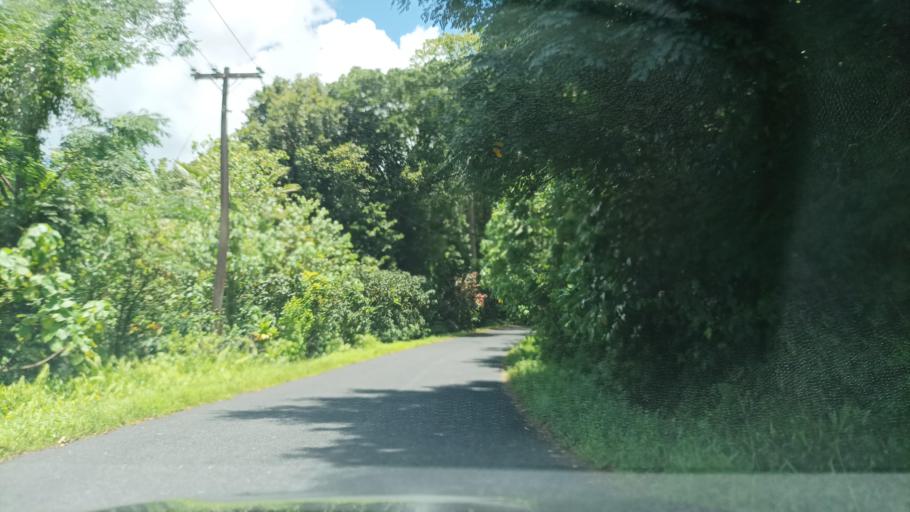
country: FM
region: Pohnpei
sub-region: Madolenihm Municipality
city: Madolenihm Municipality Government
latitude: 6.8605
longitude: 158.2935
